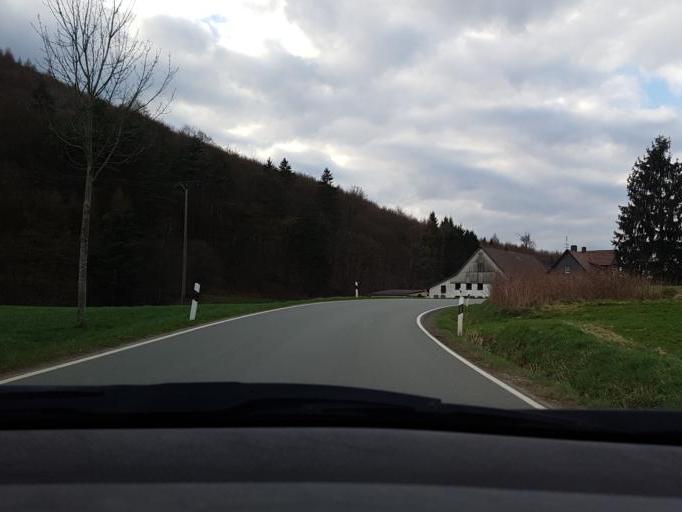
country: DE
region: Lower Saxony
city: Bodenfelde
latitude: 51.6673
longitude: 9.5416
